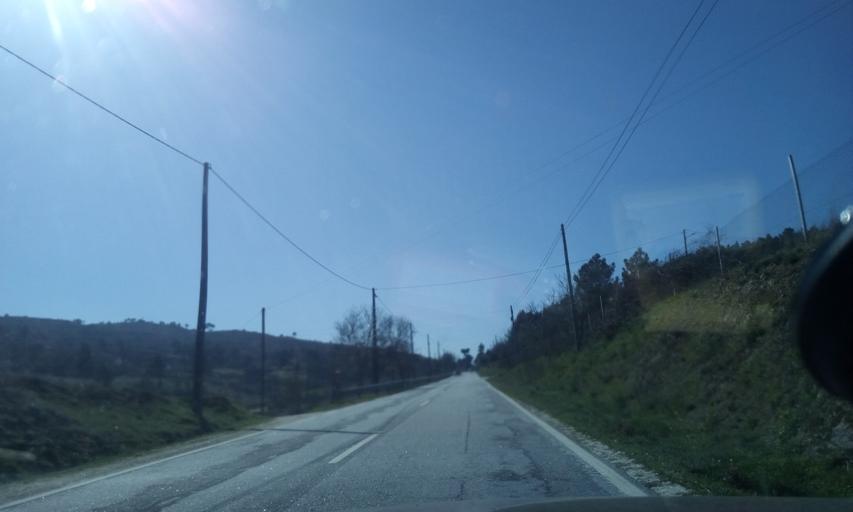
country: PT
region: Guarda
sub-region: Celorico da Beira
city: Celorico da Beira
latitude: 40.6125
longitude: -7.4147
